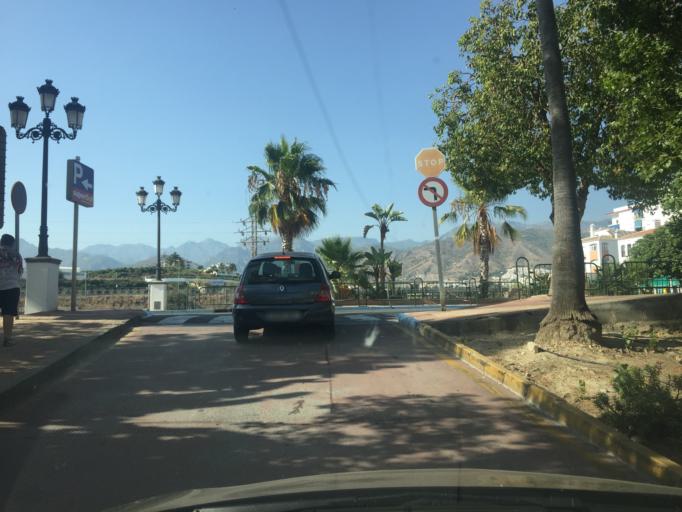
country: ES
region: Andalusia
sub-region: Provincia de Malaga
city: Nerja
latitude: 36.7478
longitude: -3.8814
